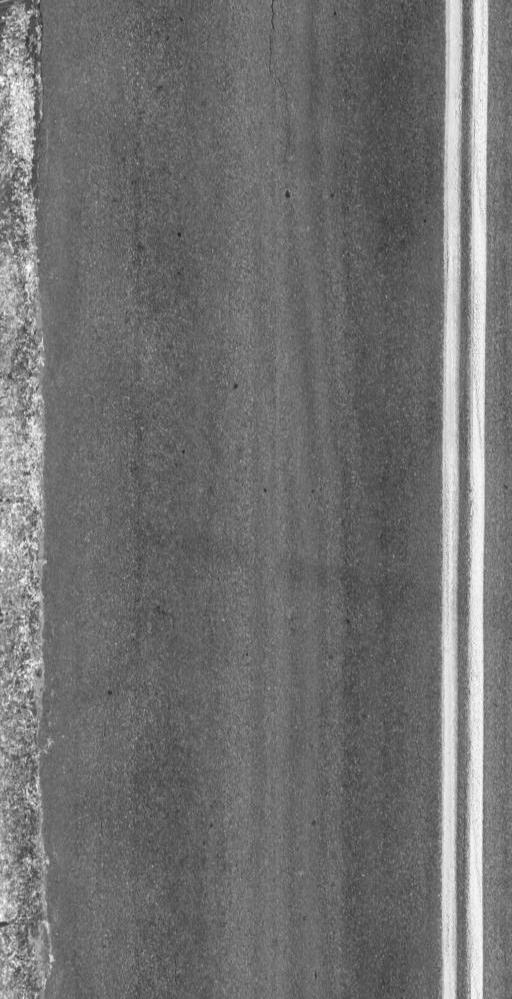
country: US
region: Vermont
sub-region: Chittenden County
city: Burlington
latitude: 44.3689
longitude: -73.2243
